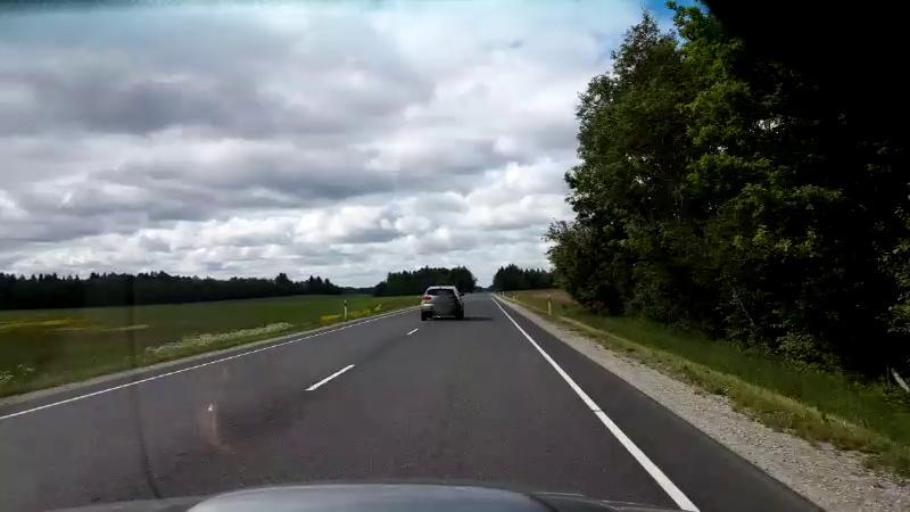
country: EE
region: Raplamaa
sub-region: Maerjamaa vald
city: Marjamaa
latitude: 58.8588
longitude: 24.4351
